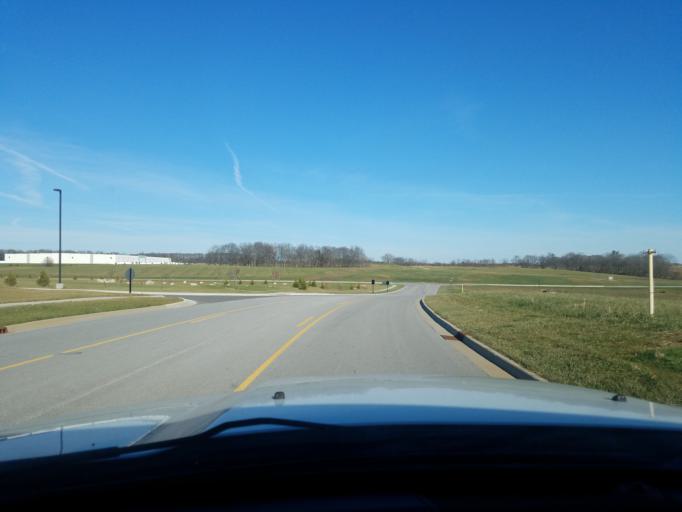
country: US
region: Indiana
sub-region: Clark County
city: Charlestown
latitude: 38.3856
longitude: -85.6762
